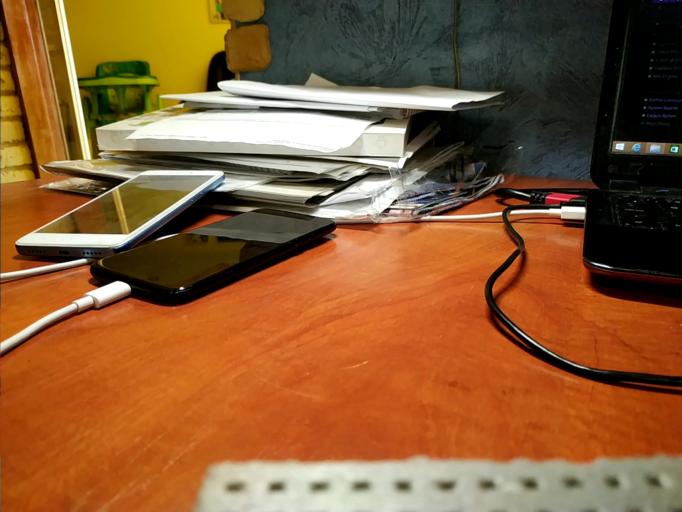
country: RU
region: Tverskaya
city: Spirovo
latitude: 57.4211
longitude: 35.1044
